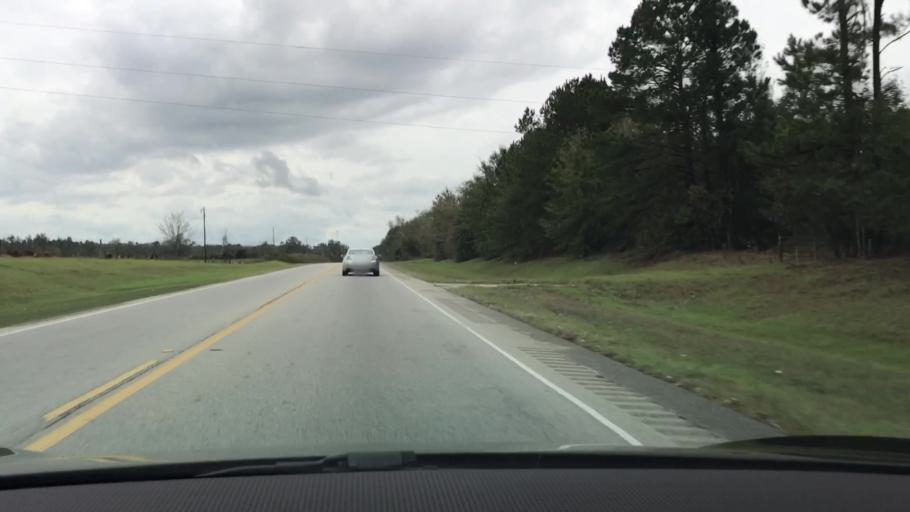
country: US
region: Georgia
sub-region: Jefferson County
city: Wadley
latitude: 32.9346
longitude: -82.3963
